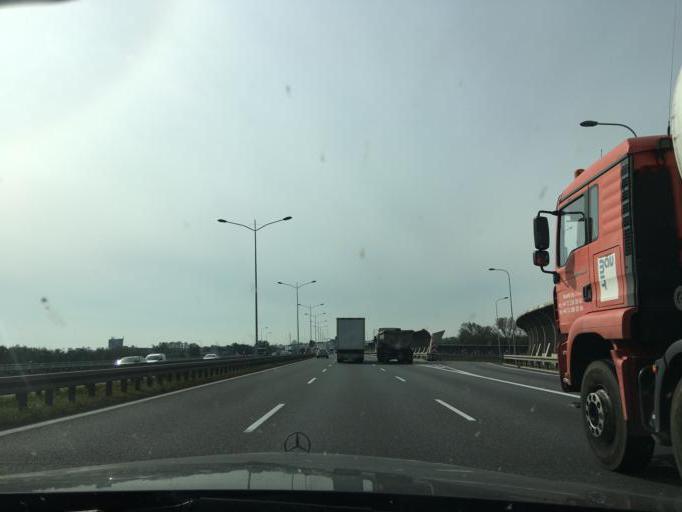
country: PL
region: Lower Silesian Voivodeship
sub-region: Powiat wroclawski
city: Smolec
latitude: 51.1344
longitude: 16.9355
